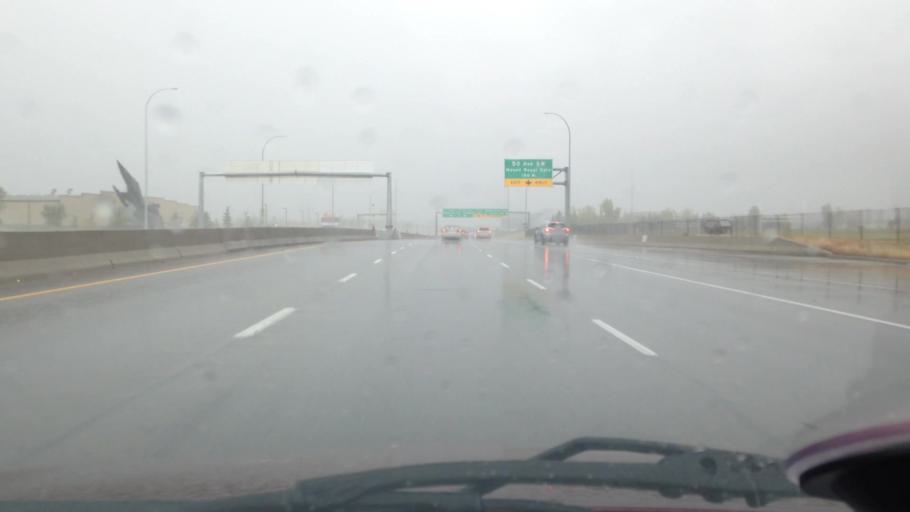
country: CA
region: Alberta
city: Calgary
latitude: 51.0139
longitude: -114.1182
